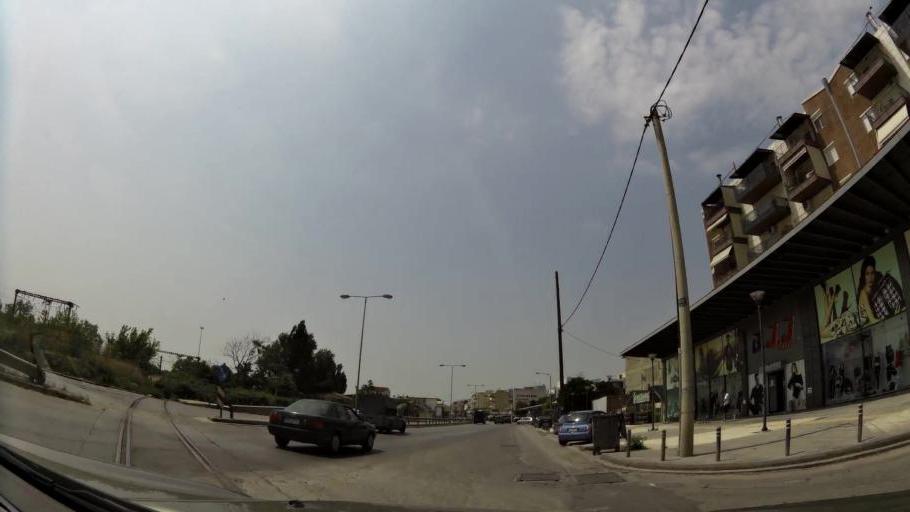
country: GR
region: Central Macedonia
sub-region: Nomos Thessalonikis
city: Menemeni
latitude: 40.6636
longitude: 22.8966
